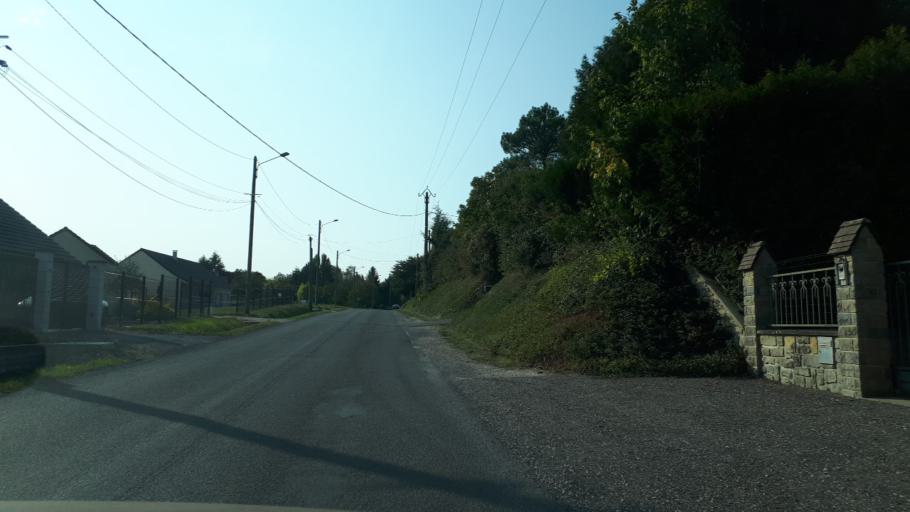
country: FR
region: Centre
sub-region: Departement du Cher
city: Vasselay
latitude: 47.2054
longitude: 2.4090
